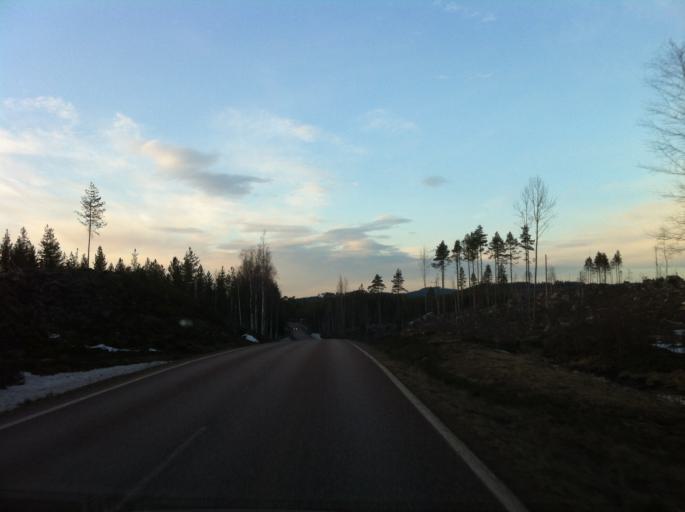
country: SE
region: Dalarna
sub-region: Vansbro Kommun
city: Vansbro
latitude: 60.5865
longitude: 14.1781
